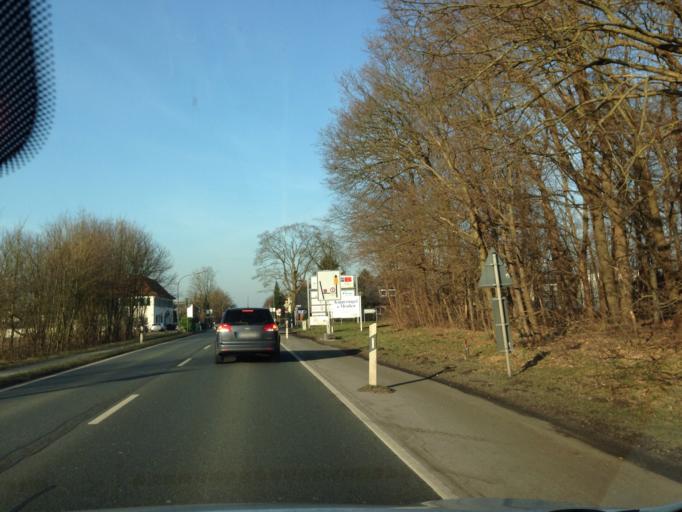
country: DE
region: North Rhine-Westphalia
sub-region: Regierungsbezirk Munster
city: Muenster
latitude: 52.0067
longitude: 7.6149
